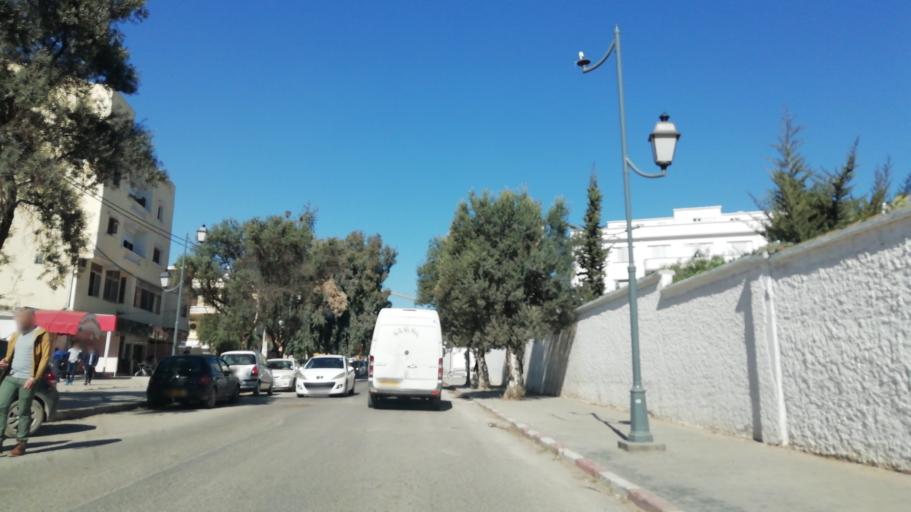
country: DZ
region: Oran
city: Oran
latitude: 35.6944
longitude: -0.6110
